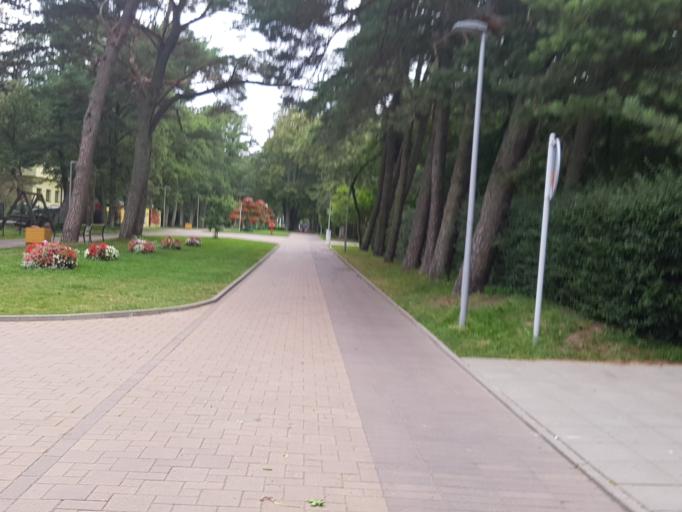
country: LT
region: Klaipedos apskritis
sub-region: Klaipeda
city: Palanga
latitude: 55.9163
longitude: 21.0526
